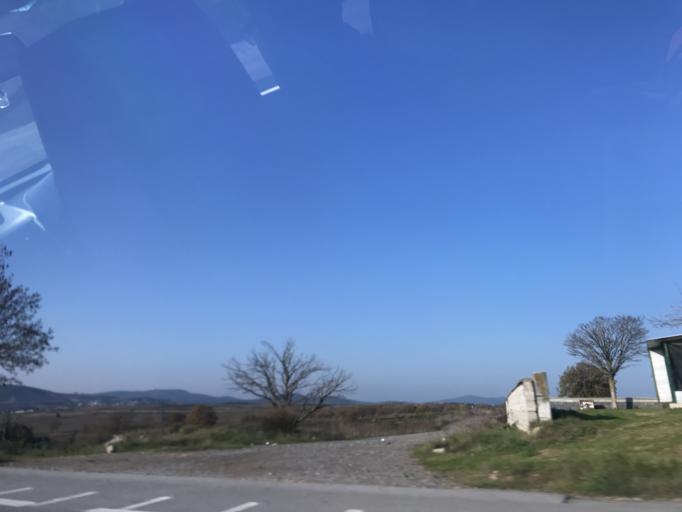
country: TR
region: Kocaeli
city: Balcik
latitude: 40.9424
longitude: 29.3732
